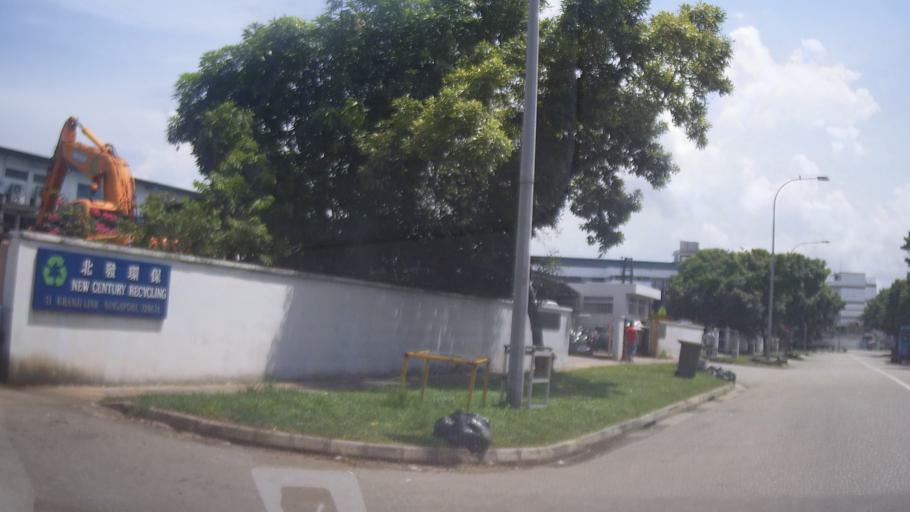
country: MY
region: Johor
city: Johor Bahru
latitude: 1.4342
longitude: 103.7464
